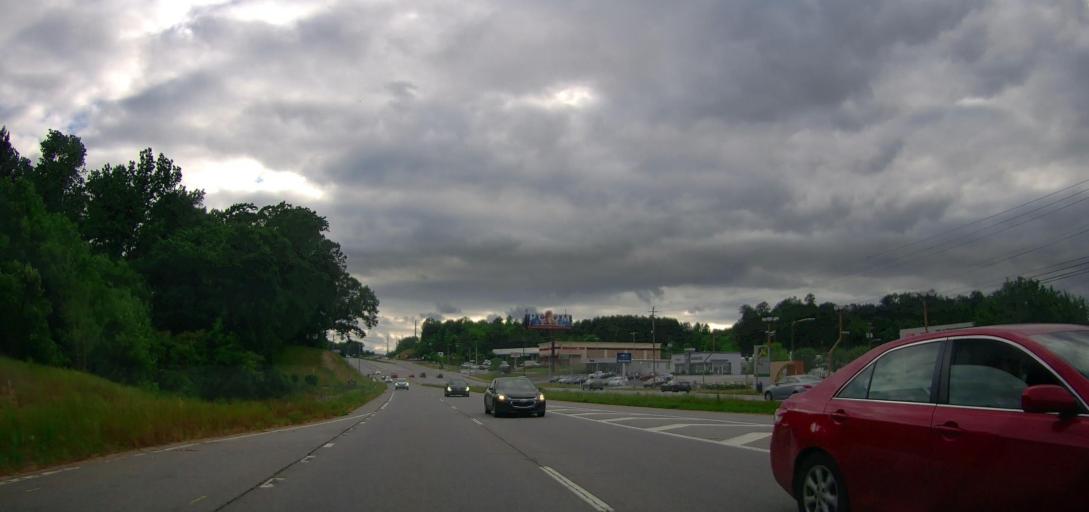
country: US
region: Georgia
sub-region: Clarke County
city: Country Club Estates
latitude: 33.9443
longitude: -83.4385
